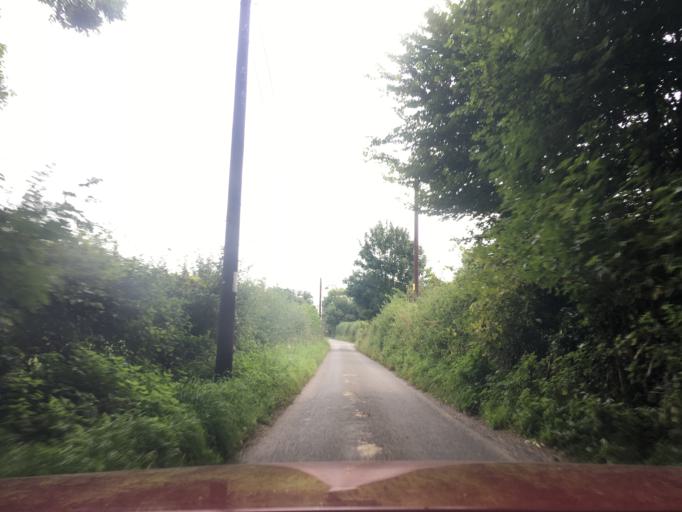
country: GB
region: England
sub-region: South Gloucestershire
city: Tytherington
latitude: 51.5814
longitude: -2.4969
